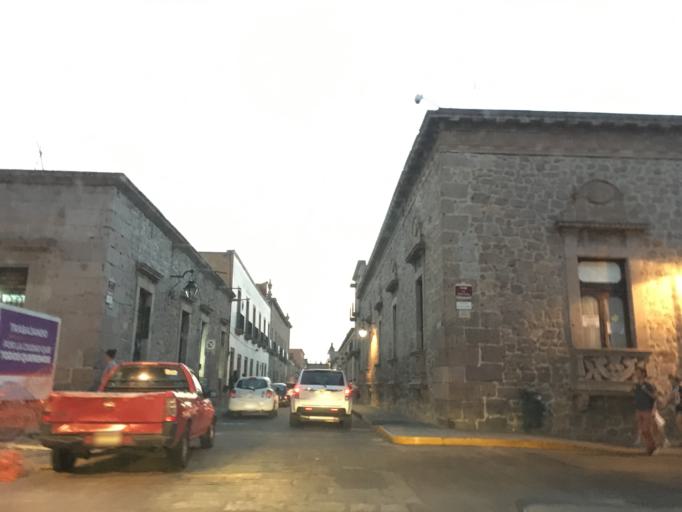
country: MX
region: Michoacan
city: Morelia
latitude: 19.7039
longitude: -101.1922
